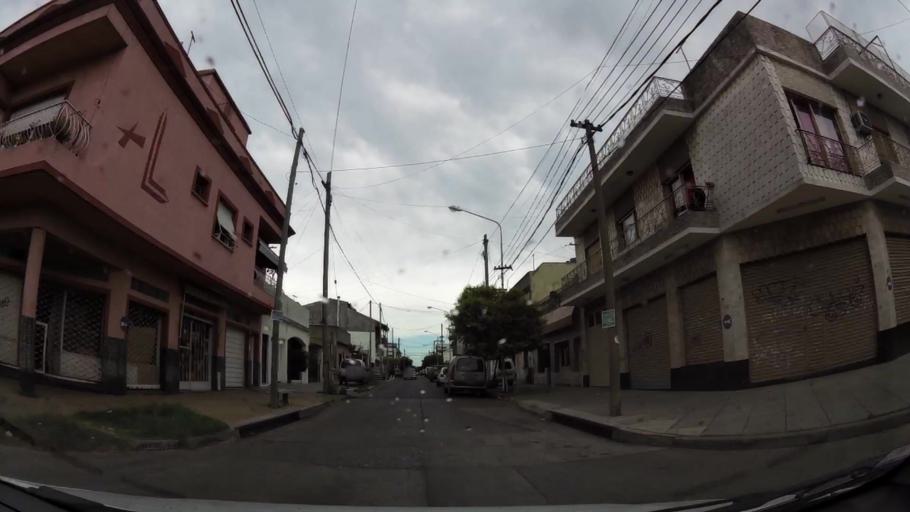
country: AR
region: Buenos Aires
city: San Justo
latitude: -34.6608
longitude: -58.5232
